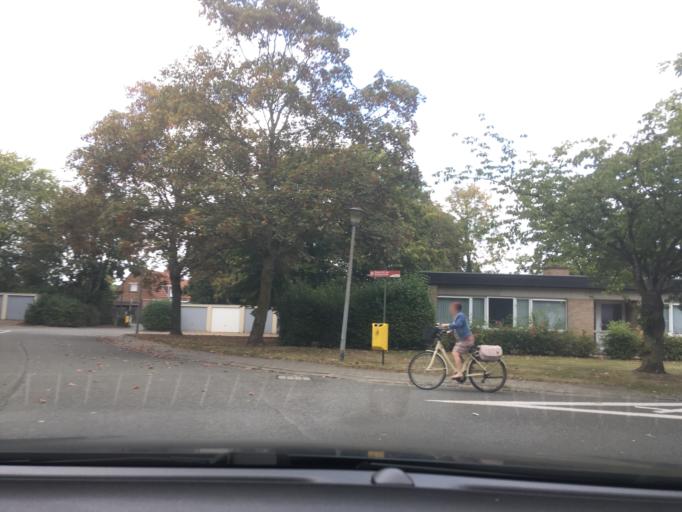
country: BE
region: Flanders
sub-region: Provincie West-Vlaanderen
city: Ieper
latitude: 50.8525
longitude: 2.9014
